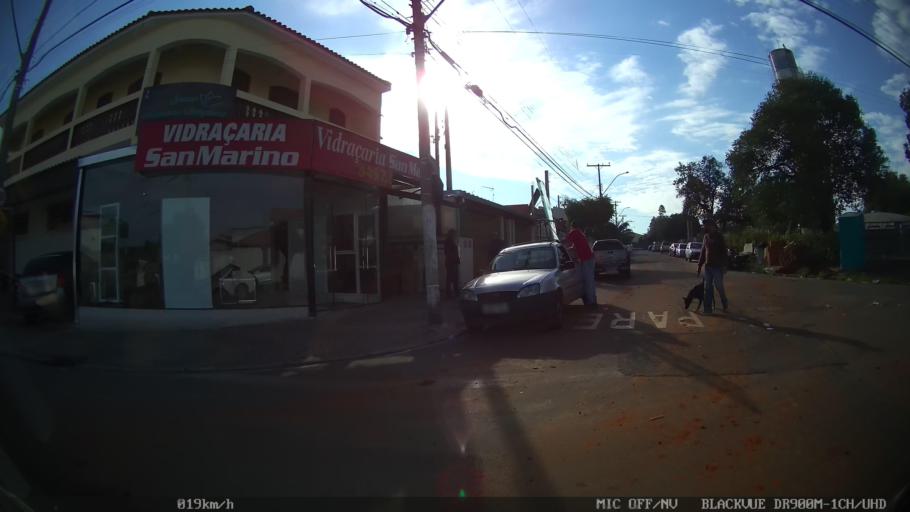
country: BR
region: Sao Paulo
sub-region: Santa Barbara D'Oeste
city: Santa Barbara d'Oeste
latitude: -22.7417
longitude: -47.3759
